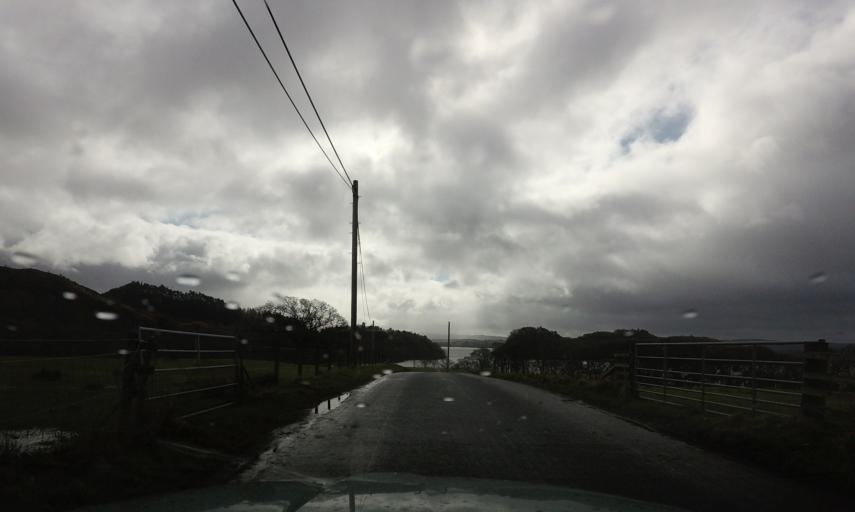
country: GB
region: Scotland
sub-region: West Dunbartonshire
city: Balloch
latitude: 56.0924
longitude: -4.5516
